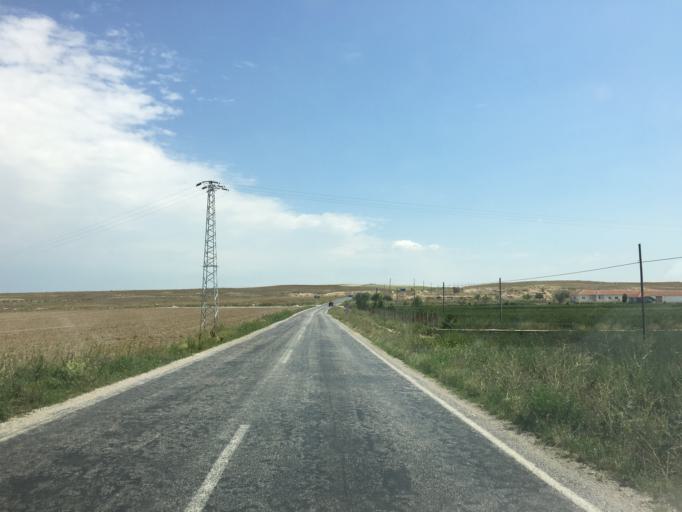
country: TR
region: Eskisehir
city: Cifteler
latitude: 39.3865
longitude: 31.0497
